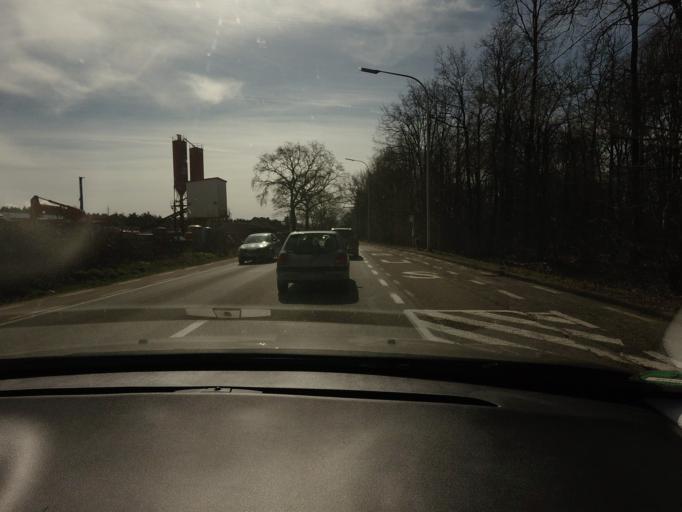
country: BE
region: Flanders
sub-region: Provincie Limburg
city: Helchteren
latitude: 51.0777
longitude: 5.3796
